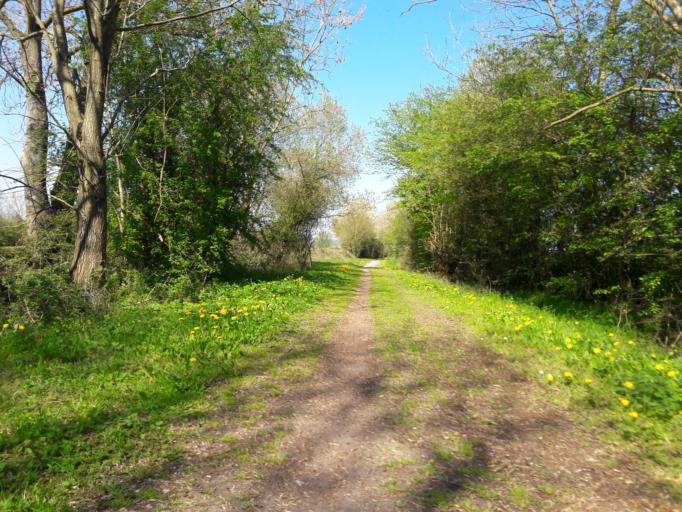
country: FR
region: Nord-Pas-de-Calais
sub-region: Departement du Nord
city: Sains-du-Nord
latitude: 50.1651
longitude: 4.0731
